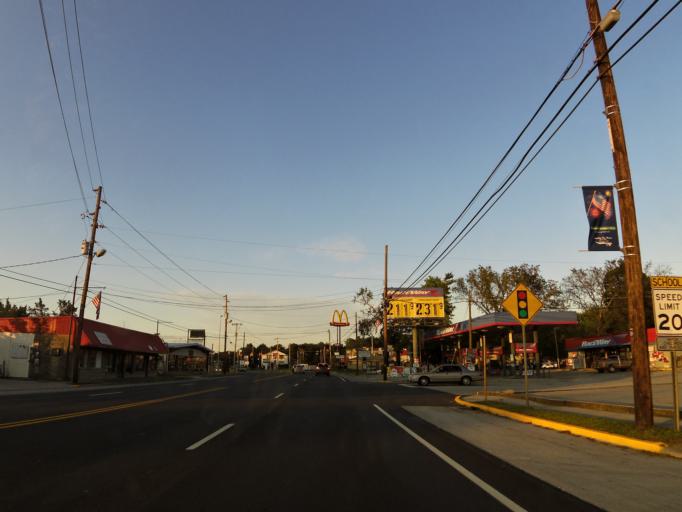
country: US
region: Tennessee
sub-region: Roane County
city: Kingston
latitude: 35.8773
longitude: -84.5116
